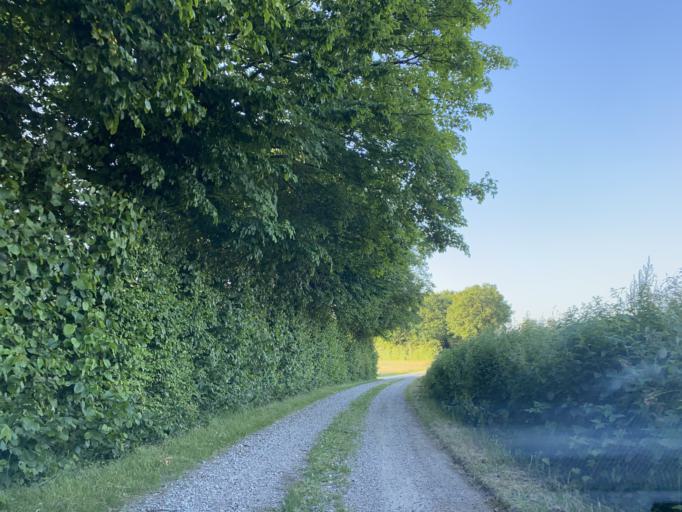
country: DK
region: South Denmark
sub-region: Haderslev Kommune
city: Starup
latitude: 55.1693
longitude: 9.5132
